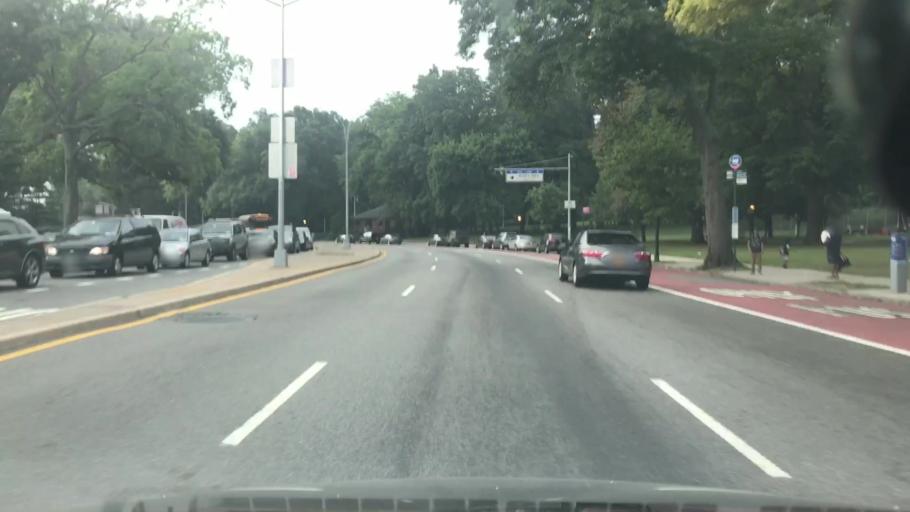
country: US
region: New York
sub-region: Queens County
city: Borough of Queens
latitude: 40.7022
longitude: -73.8554
